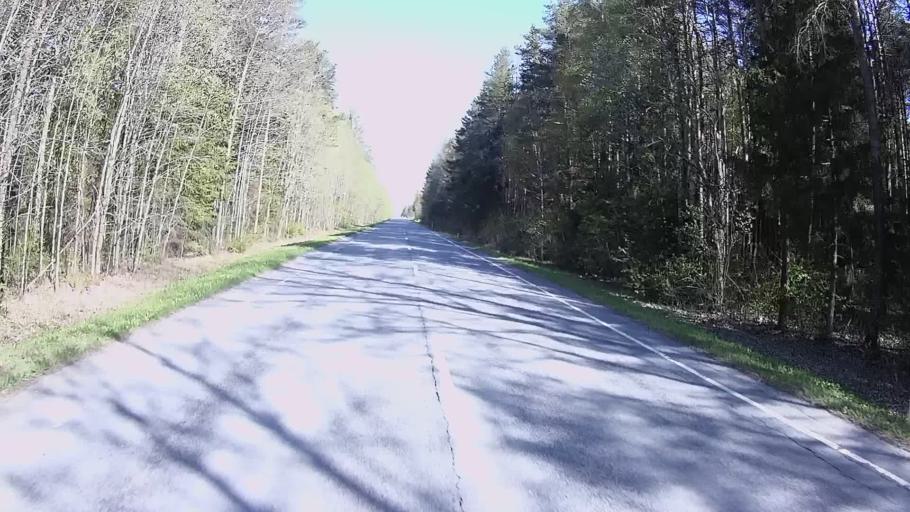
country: EE
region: Raplamaa
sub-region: Jaervakandi vald
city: Jarvakandi
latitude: 58.8508
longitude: 24.7946
